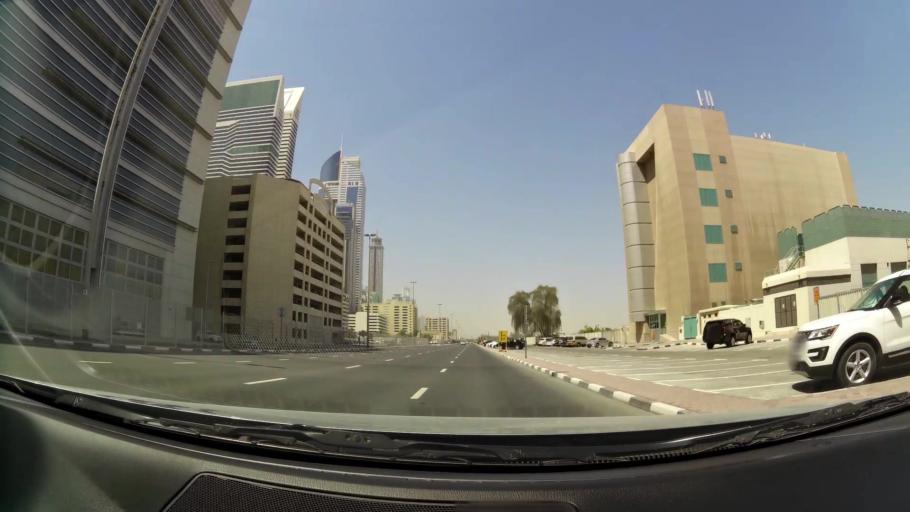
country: AE
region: Ash Shariqah
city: Sharjah
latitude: 25.2268
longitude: 55.2826
